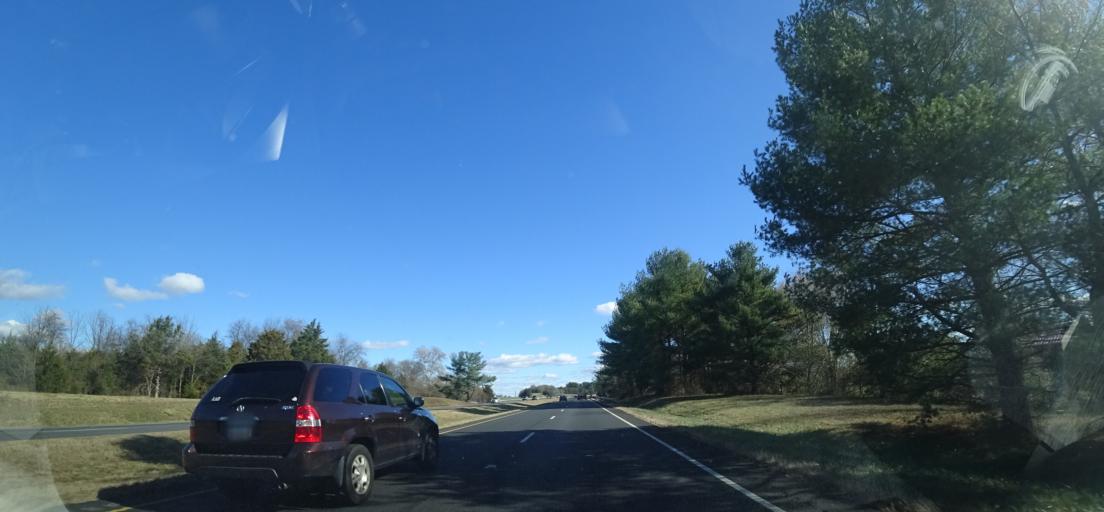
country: US
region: Virginia
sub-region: Culpeper County
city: Culpeper
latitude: 38.5028
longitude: -77.9009
